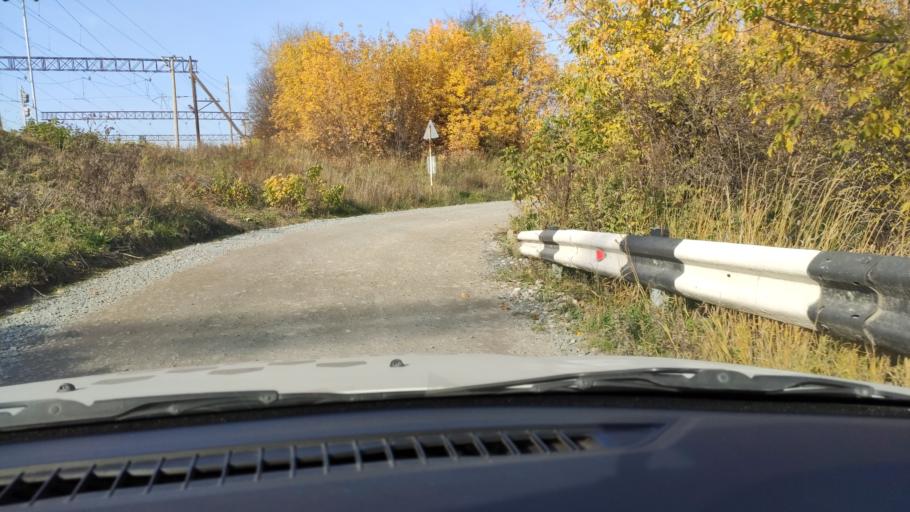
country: RU
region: Perm
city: Sylva
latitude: 58.0432
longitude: 56.7467
